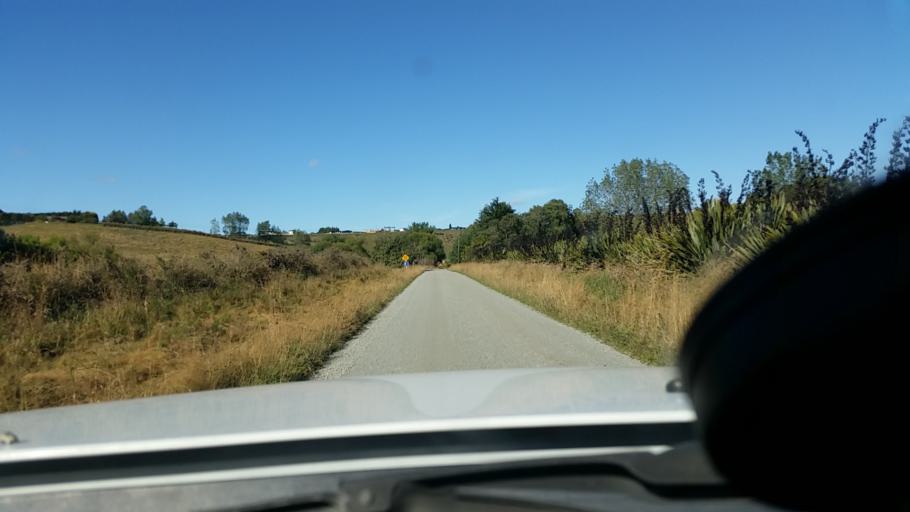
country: NZ
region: Canterbury
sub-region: Timaru District
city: Pleasant Point
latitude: -44.3432
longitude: 171.1604
